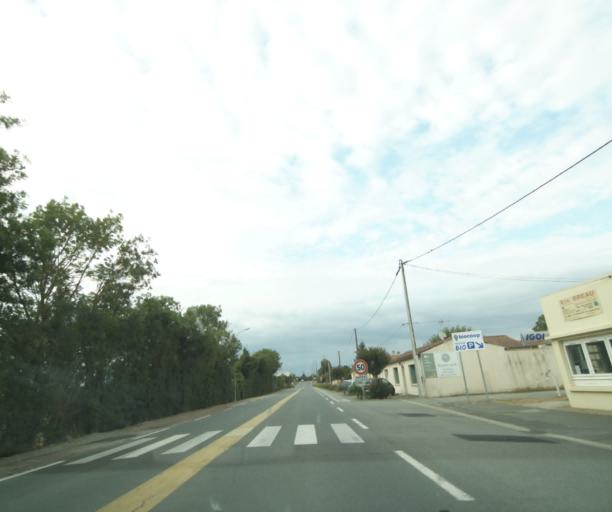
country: FR
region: Poitou-Charentes
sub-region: Departement de la Charente-Maritime
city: Marans
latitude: 46.2997
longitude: -0.9905
